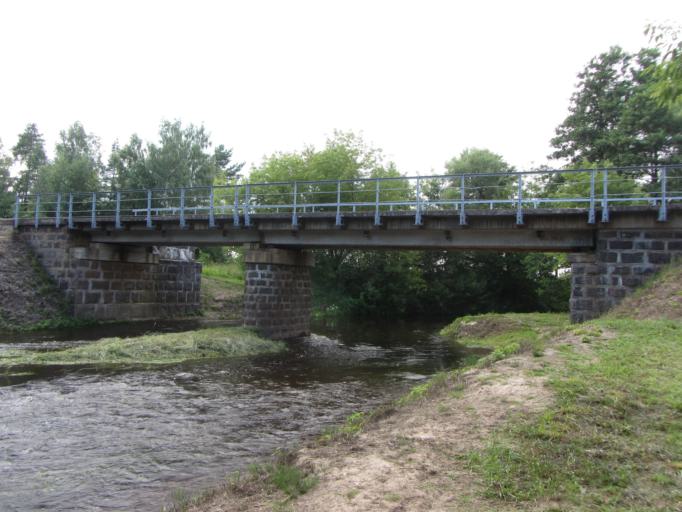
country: LT
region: Panevezys
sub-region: Panevezys City
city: Panevezys
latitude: 55.7384
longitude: 24.2382
